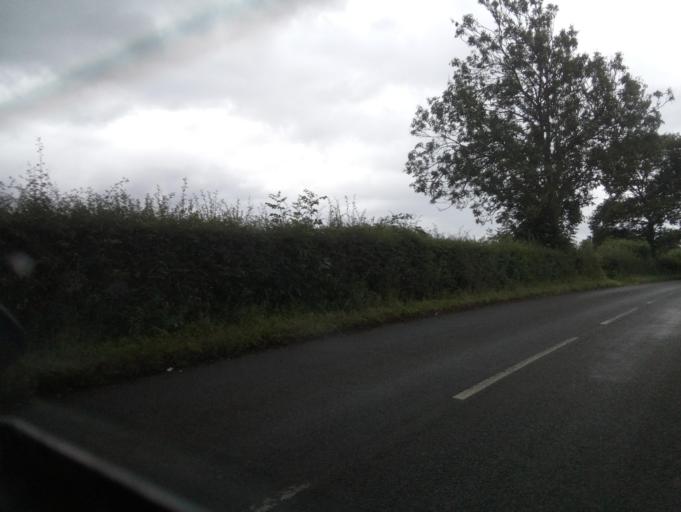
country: GB
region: England
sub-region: Solihull
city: Cheswick Green
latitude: 52.3835
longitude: -1.8221
